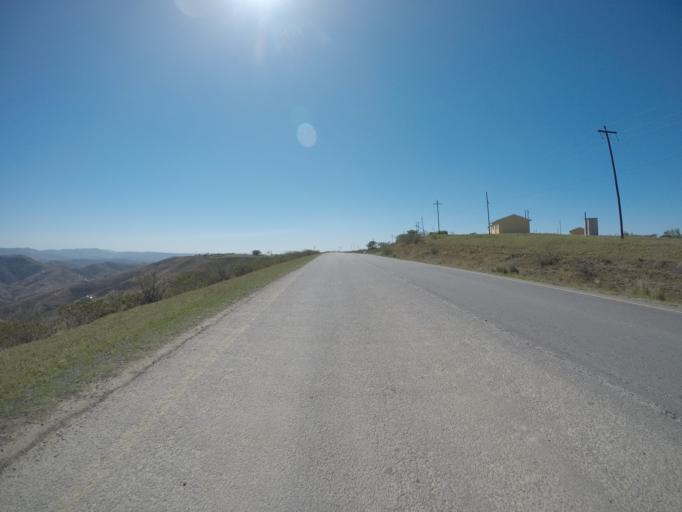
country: ZA
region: Eastern Cape
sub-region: OR Tambo District Municipality
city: Libode
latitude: -31.9130
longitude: 28.9895
